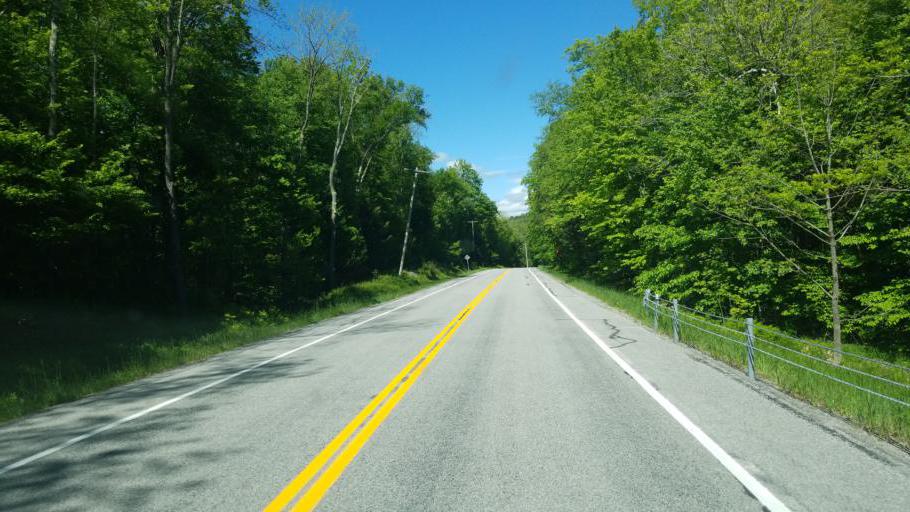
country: US
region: New York
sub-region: Fulton County
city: Gloversville
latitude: 43.1884
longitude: -74.5322
